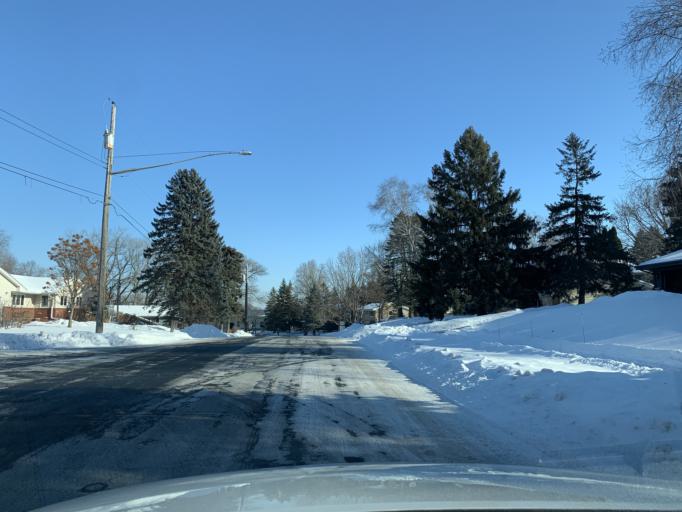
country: US
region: Minnesota
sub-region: Hennepin County
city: Bloomington
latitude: 44.8306
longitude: -93.3496
